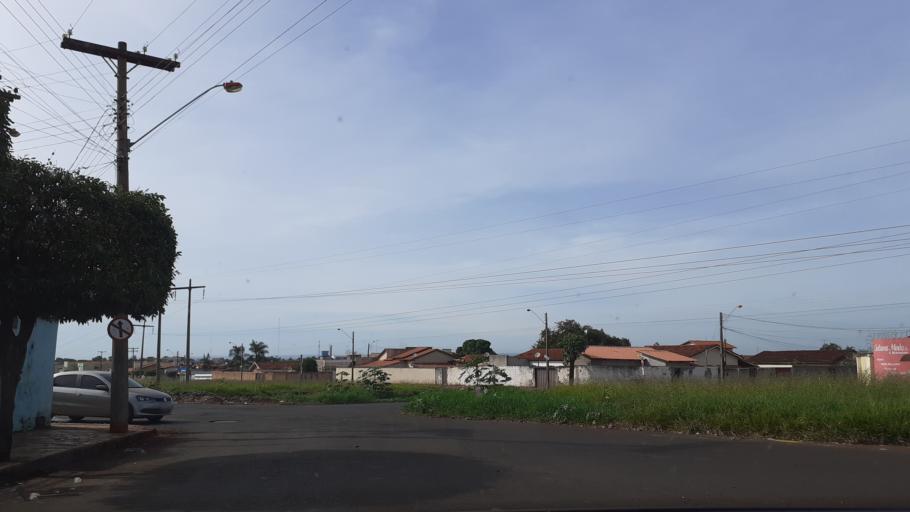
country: BR
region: Goias
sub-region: Itumbiara
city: Itumbiara
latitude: -18.4191
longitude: -49.2424
